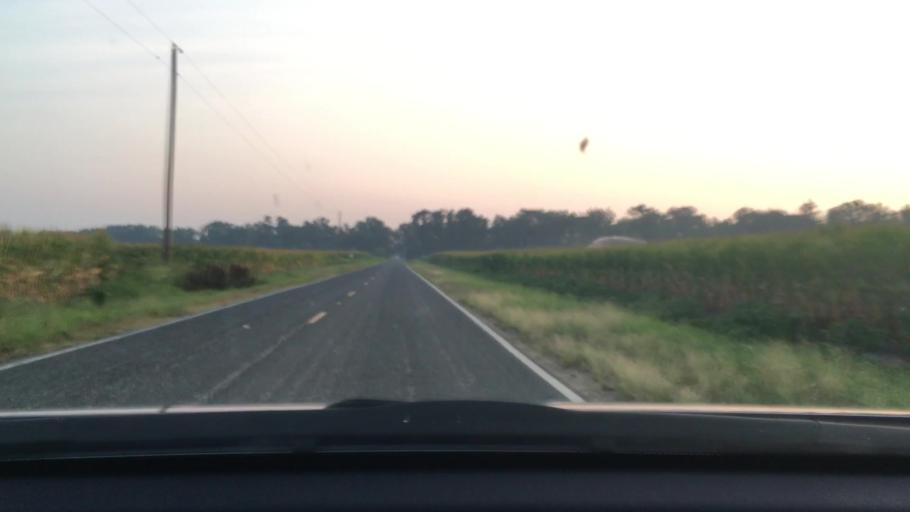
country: US
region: South Carolina
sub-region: Lee County
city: Bishopville
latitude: 34.2020
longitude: -80.1361
